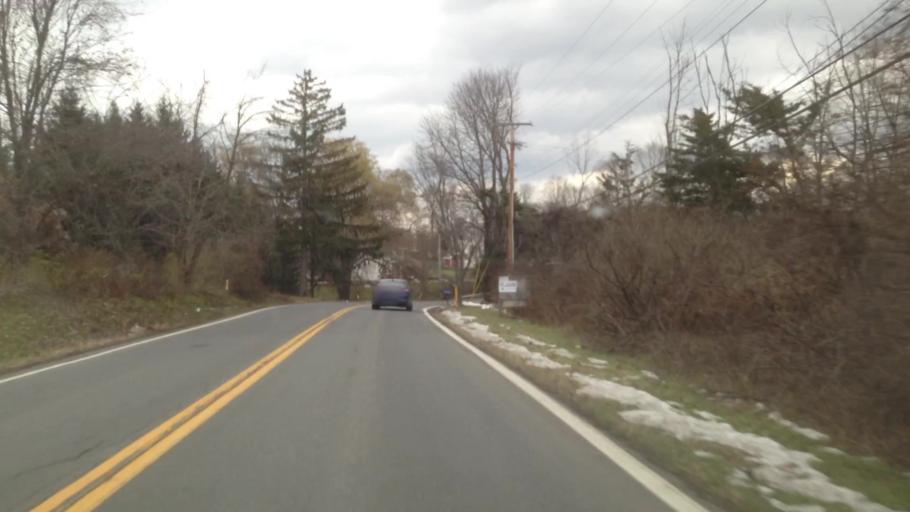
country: US
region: New York
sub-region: Ulster County
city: Glasco
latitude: 42.0375
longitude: -73.9543
